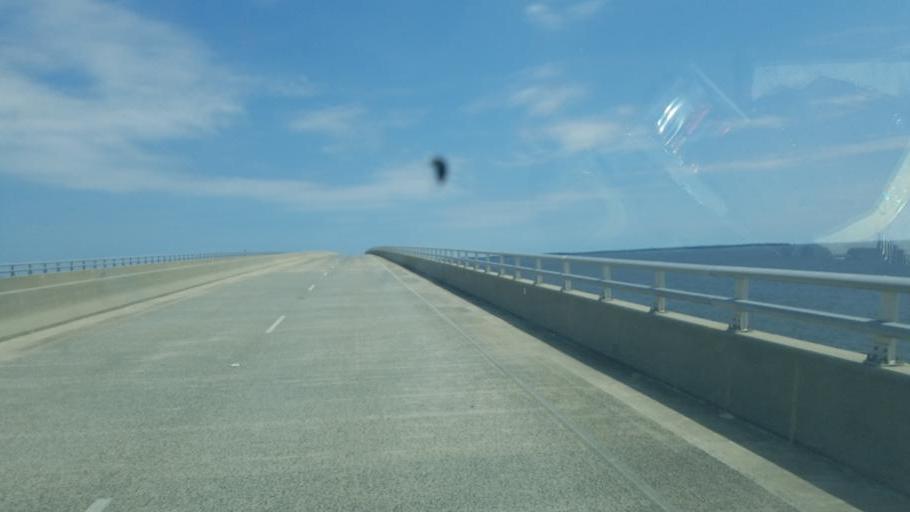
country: US
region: North Carolina
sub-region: Dare County
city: Manteo
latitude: 35.8858
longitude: -75.7209
